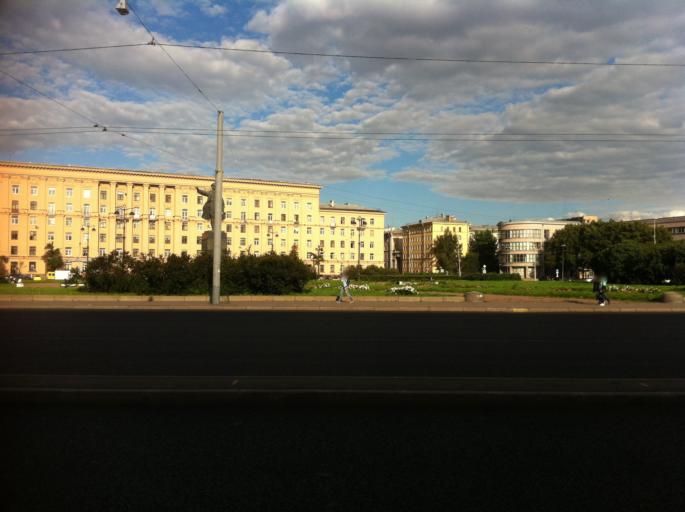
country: RU
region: St.-Petersburg
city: Admiralteisky
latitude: 59.8961
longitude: 30.2757
